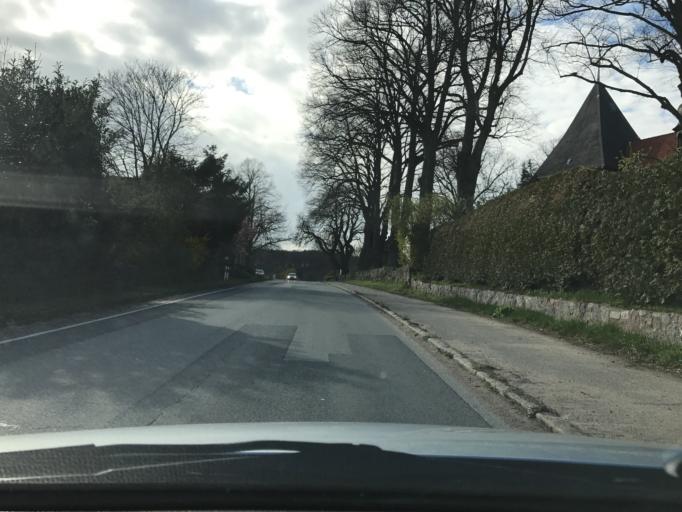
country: DE
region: Schleswig-Holstein
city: Kirchnuchel
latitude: 54.2043
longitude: 10.6790
